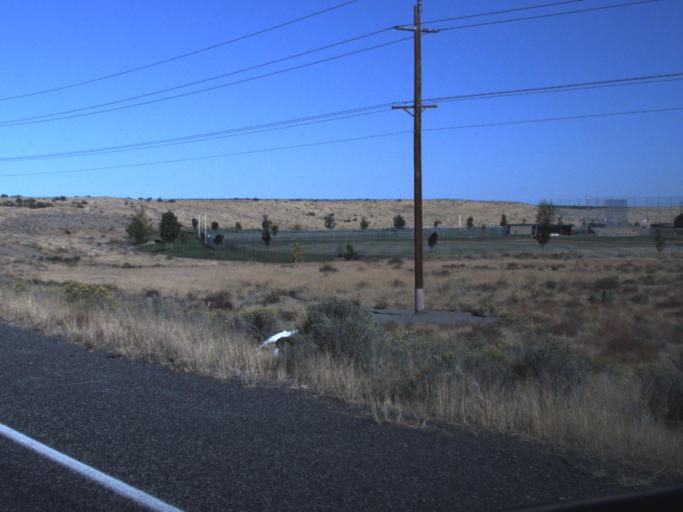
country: US
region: Washington
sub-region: Benton County
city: West Richland
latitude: 46.3286
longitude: -119.3225
